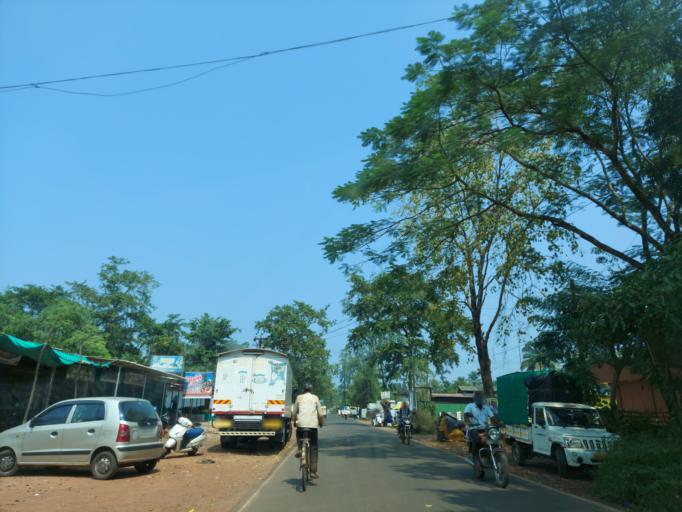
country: IN
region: Maharashtra
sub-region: Sindhudurg
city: Kudal
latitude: 15.9888
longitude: 73.6832
